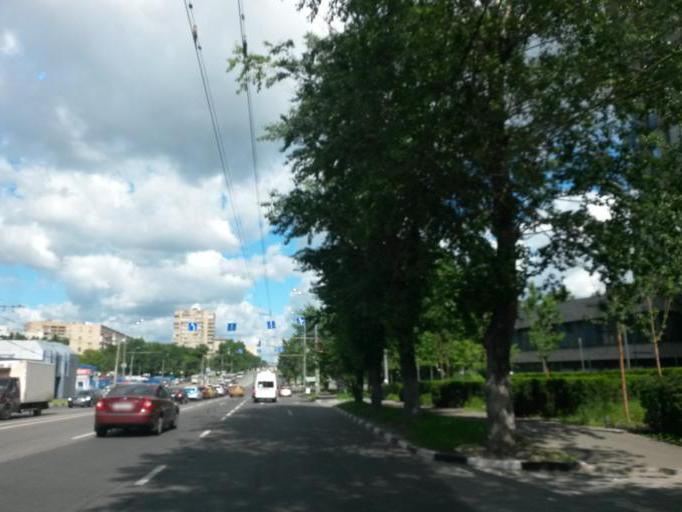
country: RU
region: Moskovskaya
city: Semenovskoye
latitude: 55.6833
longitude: 37.5539
